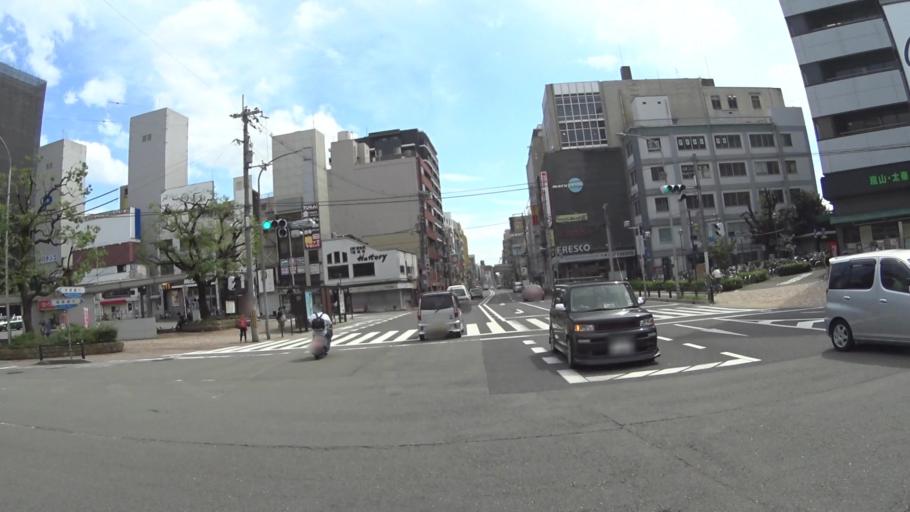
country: JP
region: Kyoto
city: Kyoto
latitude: 35.0037
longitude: 135.7489
